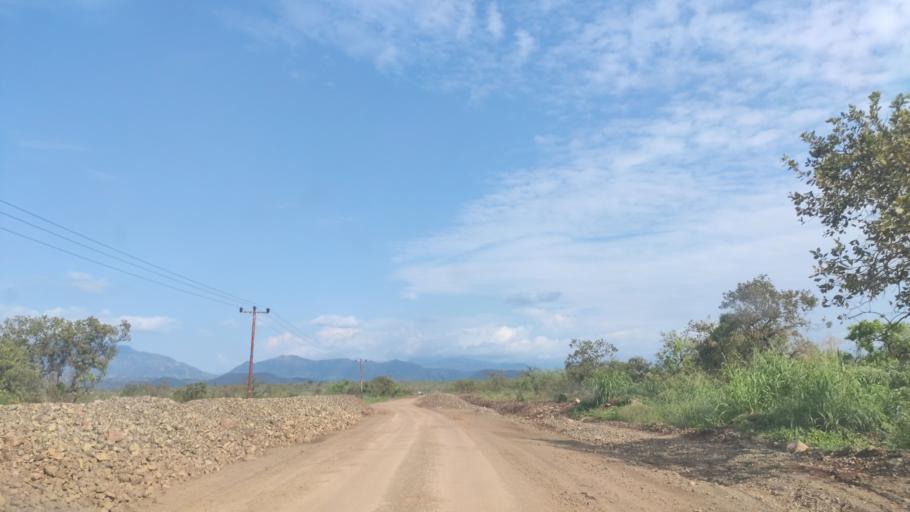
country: ET
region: Southern Nations, Nationalities, and People's Region
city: Felege Neway
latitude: 6.4253
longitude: 37.2325
